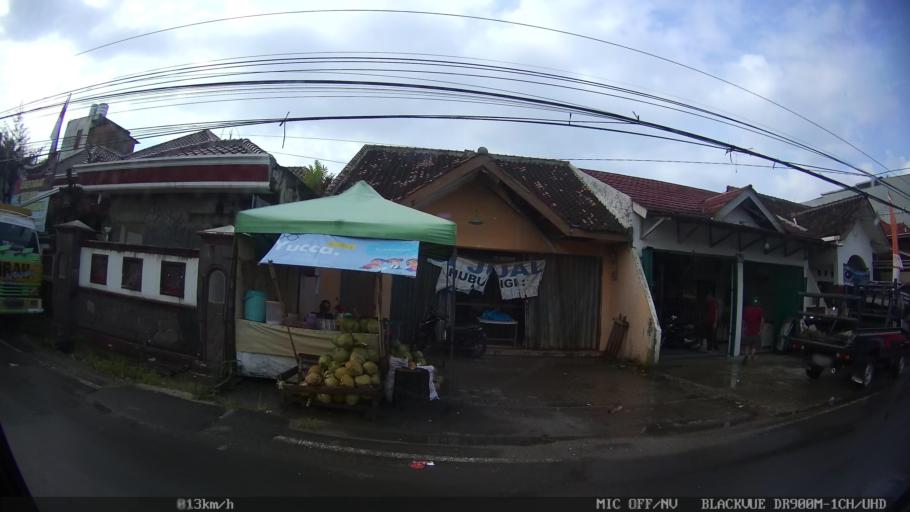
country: ID
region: Lampung
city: Kedaton
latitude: -5.3911
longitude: 105.3013
